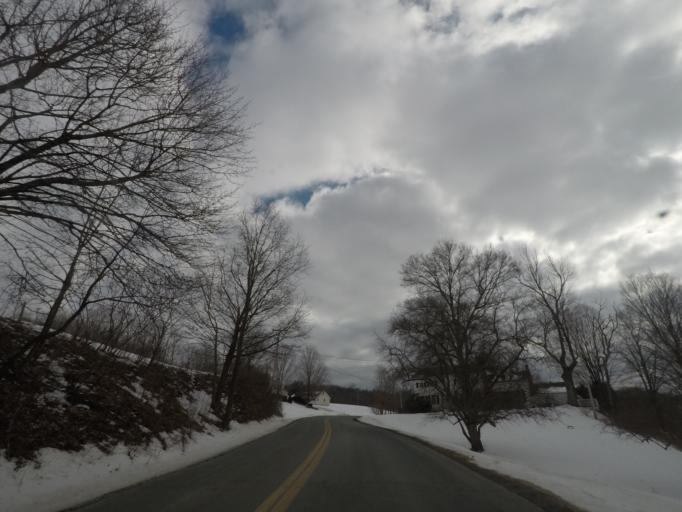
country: US
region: New York
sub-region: Rensselaer County
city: Hoosick Falls
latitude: 42.8955
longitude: -73.4203
